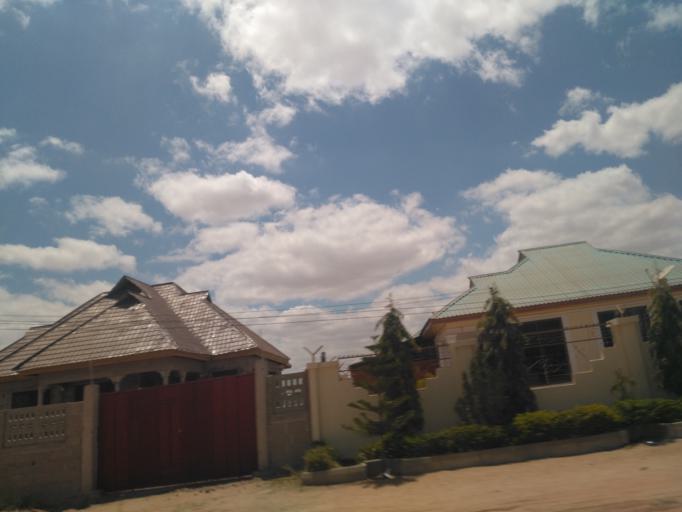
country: TZ
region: Dodoma
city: Kisasa
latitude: -6.1673
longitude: 35.7983
